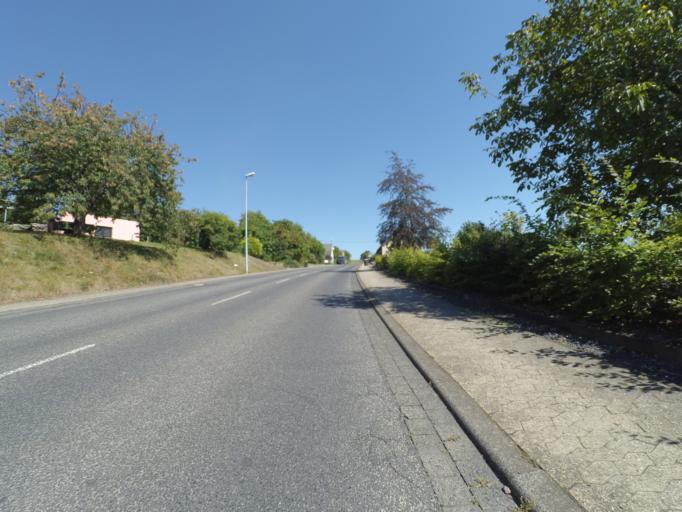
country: DE
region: Rheinland-Pfalz
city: Mullenbach
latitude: 50.2225
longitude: 7.0642
